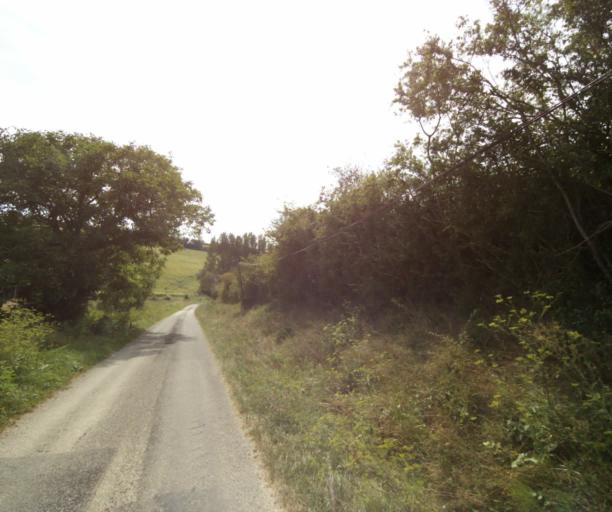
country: FR
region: Midi-Pyrenees
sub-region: Departement de la Haute-Garonne
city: Gaillac-Toulza
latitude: 43.2445
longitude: 1.4071
